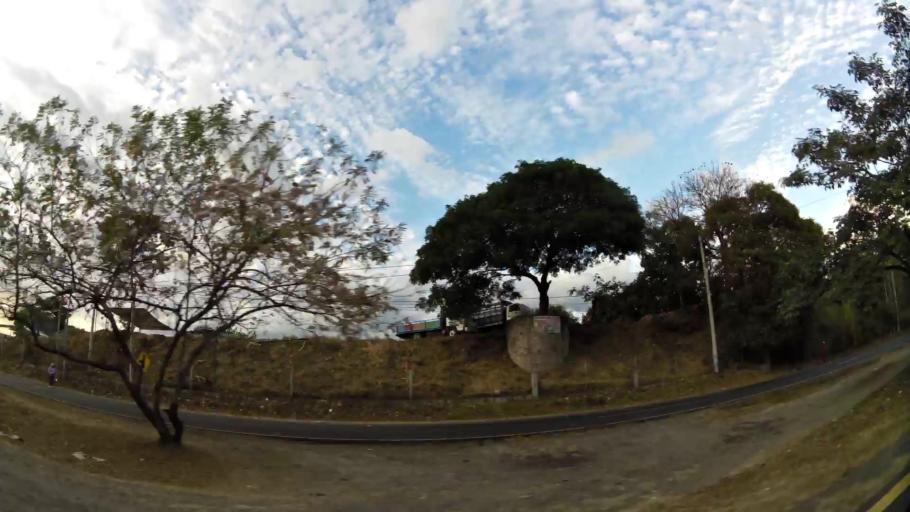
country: SV
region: San Vicente
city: San Vicente
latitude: 13.6701
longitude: -88.8339
